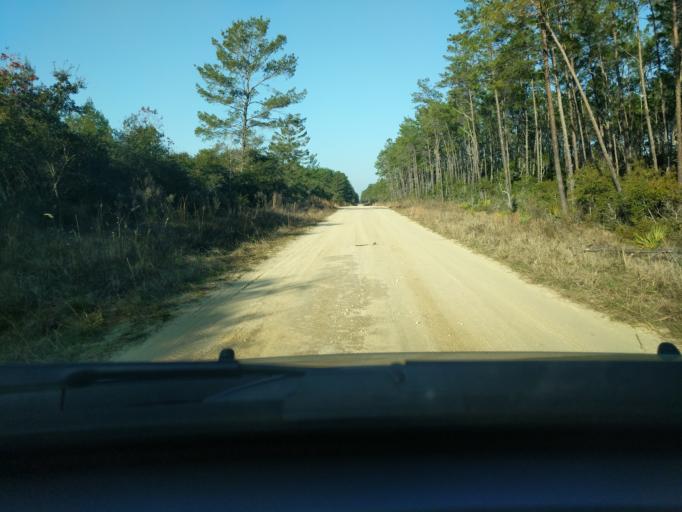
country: US
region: Florida
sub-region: Lake County
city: Astor
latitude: 29.2261
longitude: -81.7796
